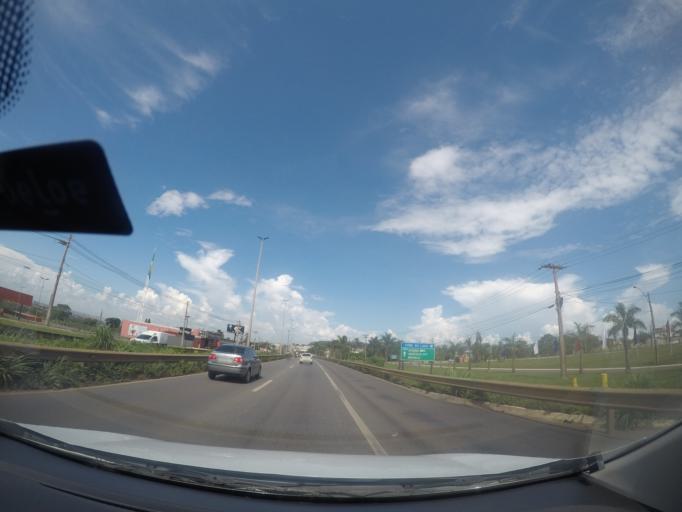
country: BR
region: Goias
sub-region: Goiania
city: Goiania
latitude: -16.6592
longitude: -49.3671
